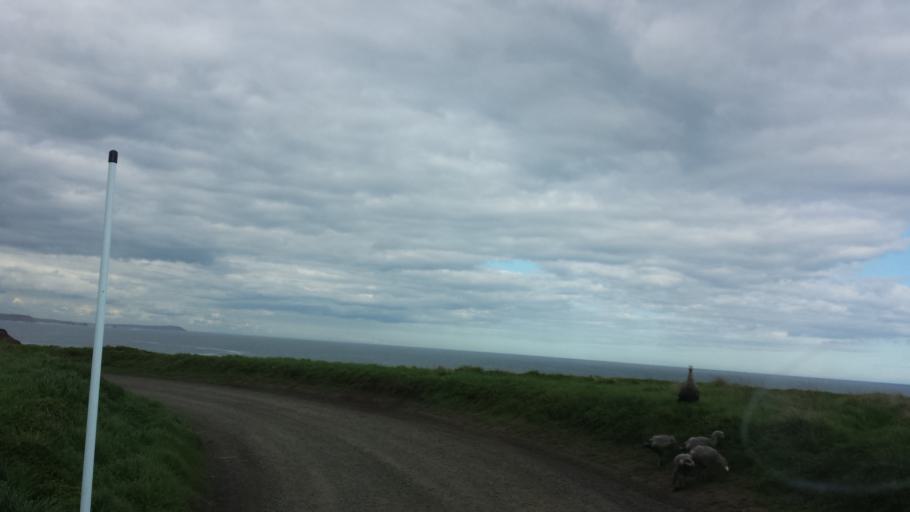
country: AU
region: Victoria
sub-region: Bass Coast
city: Phillip Island
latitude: -38.5165
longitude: 145.1304
